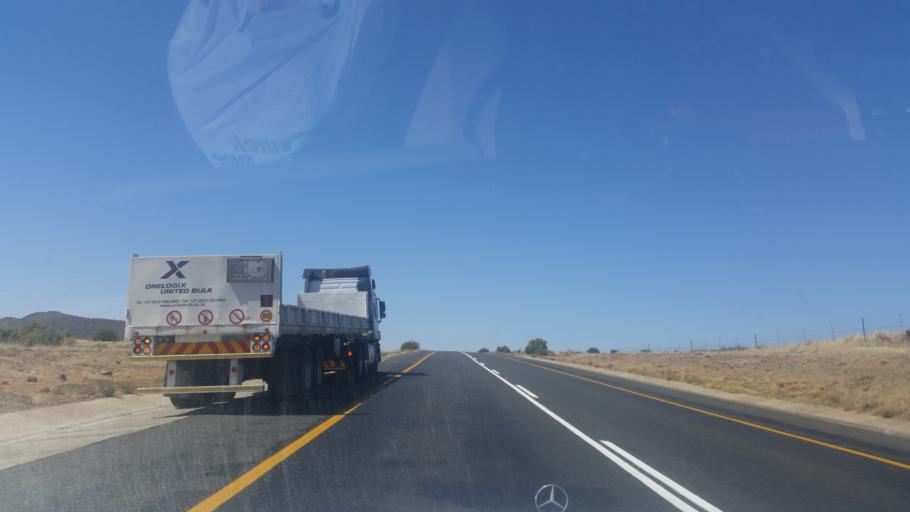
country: ZA
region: Northern Cape
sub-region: Pixley ka Seme District Municipality
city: Colesberg
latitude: -30.5831
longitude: 25.4236
